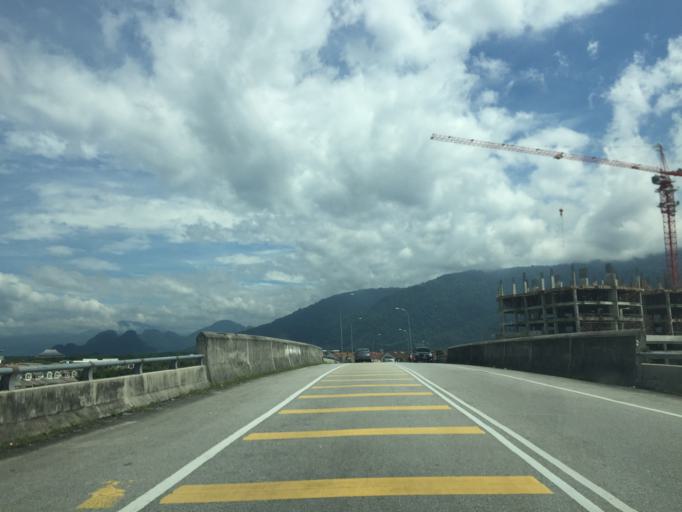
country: MY
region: Perak
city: Kampar
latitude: 4.3271
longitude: 101.1309
